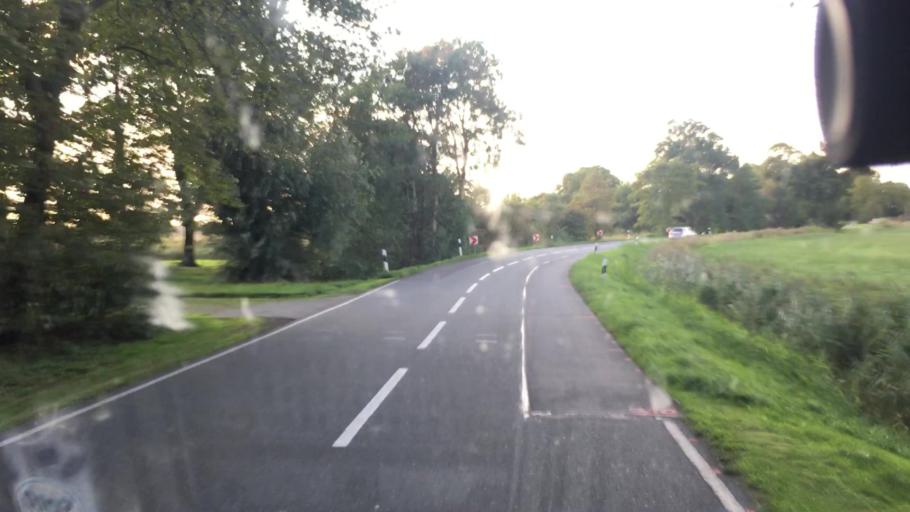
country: DE
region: Lower Saxony
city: Wittmund
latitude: 53.6400
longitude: 7.8197
